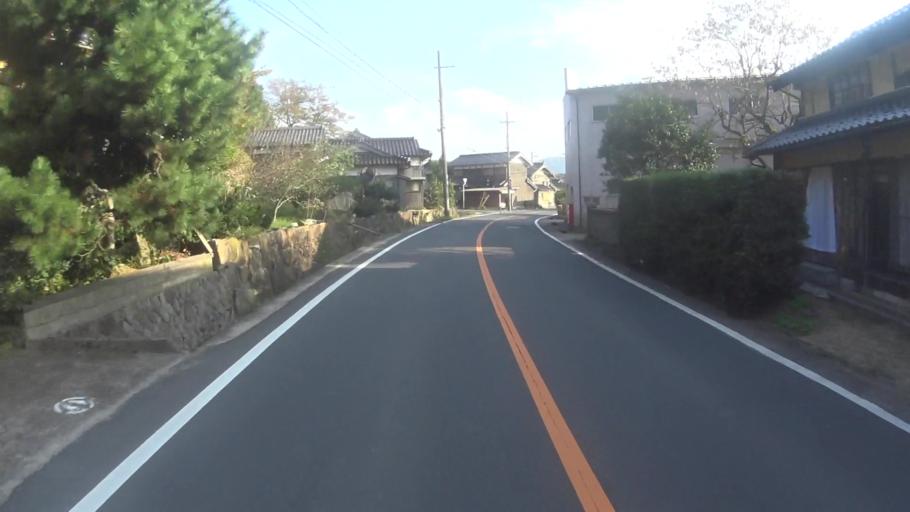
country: JP
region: Kyoto
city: Miyazu
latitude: 35.6843
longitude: 135.0990
